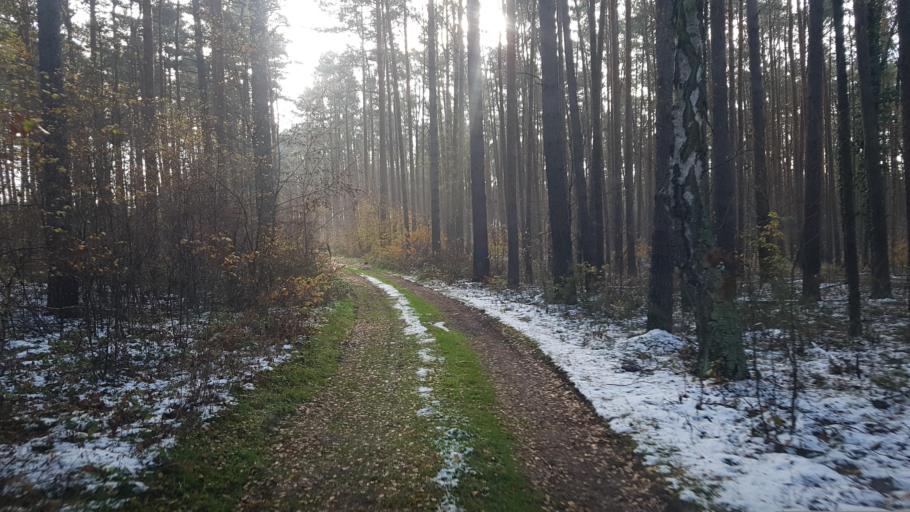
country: DE
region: Brandenburg
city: Bronkow
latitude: 51.6614
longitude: 13.8976
